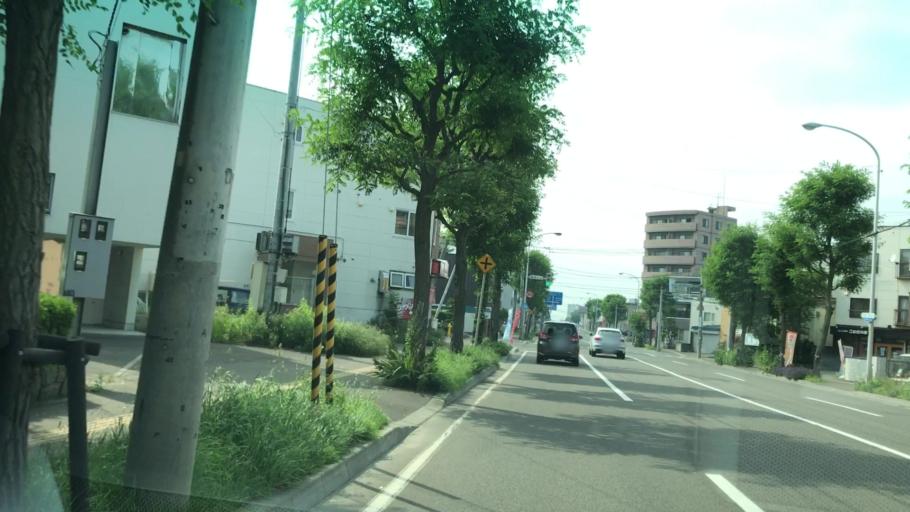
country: JP
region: Hokkaido
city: Sapporo
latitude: 43.0857
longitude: 141.2968
